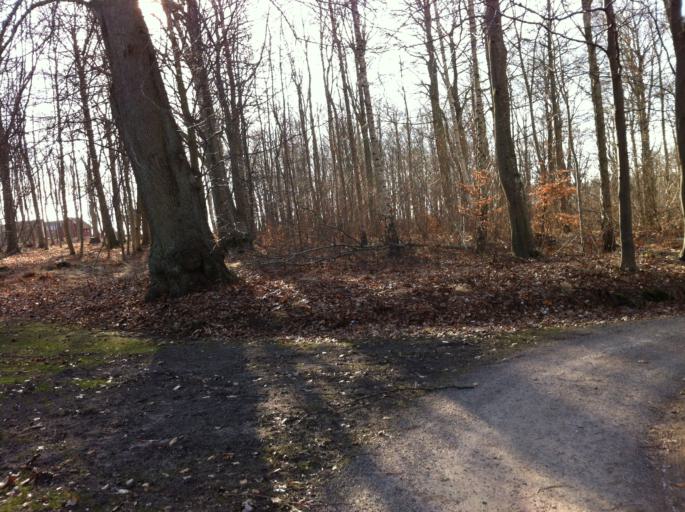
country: SE
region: Skane
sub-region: Hoganas Kommun
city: Hoganas
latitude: 56.2599
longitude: 12.5302
